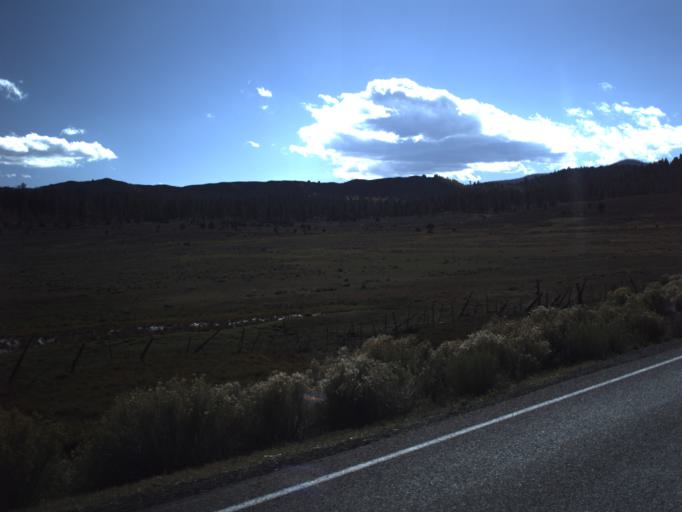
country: US
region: Utah
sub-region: Garfield County
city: Panguitch
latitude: 37.7058
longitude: -112.6364
